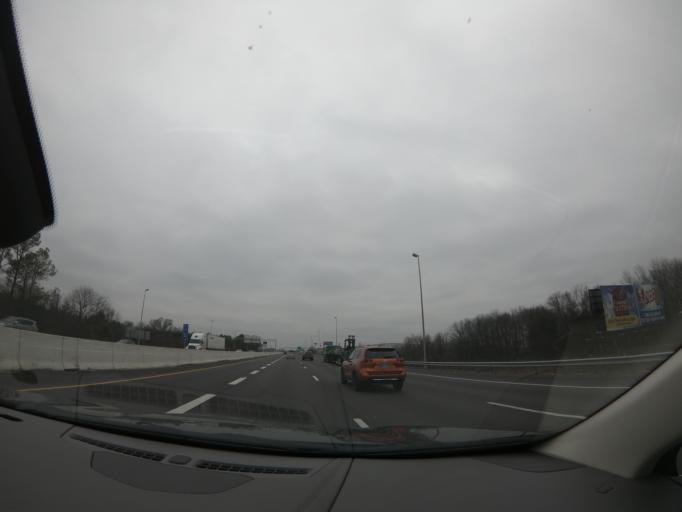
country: US
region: Tennessee
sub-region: Rutherford County
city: Murfreesboro
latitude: 35.8217
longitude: -86.4070
